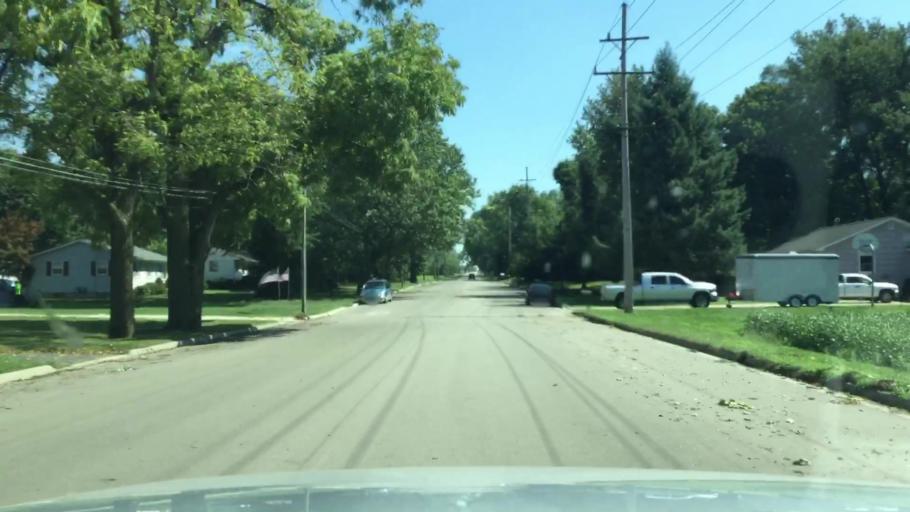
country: US
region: Michigan
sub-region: Lenawee County
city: Clinton
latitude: 42.0648
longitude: -83.9648
